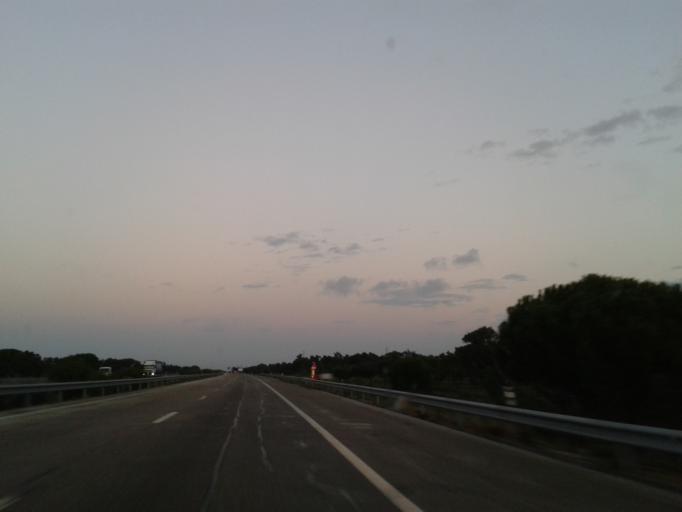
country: PT
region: Evora
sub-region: Vendas Novas
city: Vendas Novas
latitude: 38.6177
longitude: -8.5942
